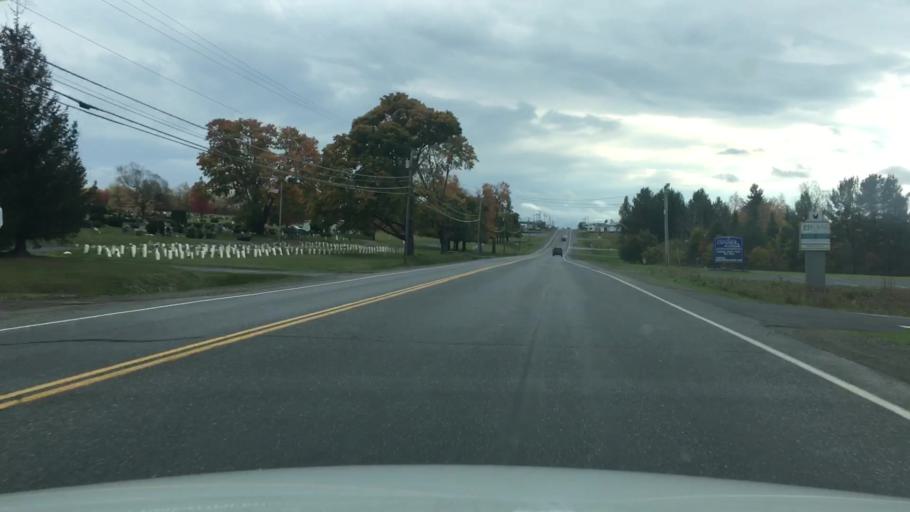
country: US
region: Maine
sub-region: Aroostook County
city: Presque Isle
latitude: 46.6644
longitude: -68.0100
